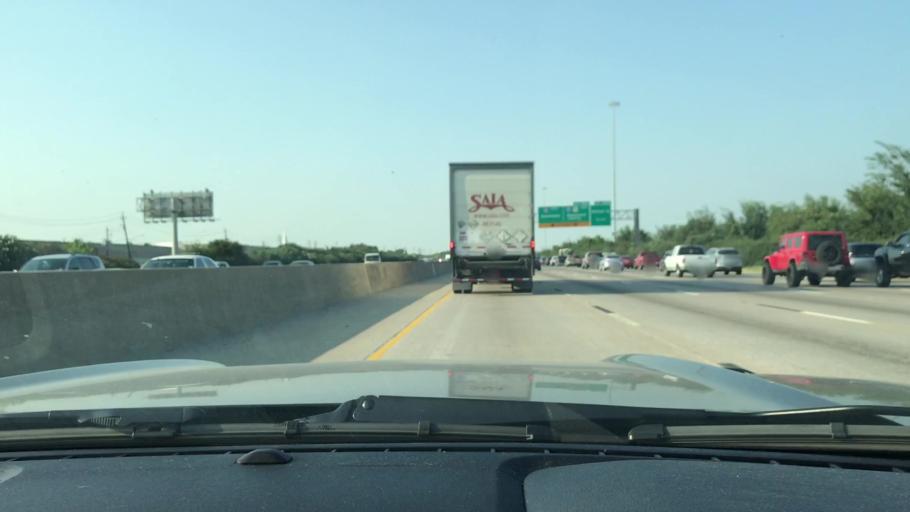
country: US
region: Texas
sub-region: Harris County
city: Jacinto City
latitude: 29.7549
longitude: -95.2650
